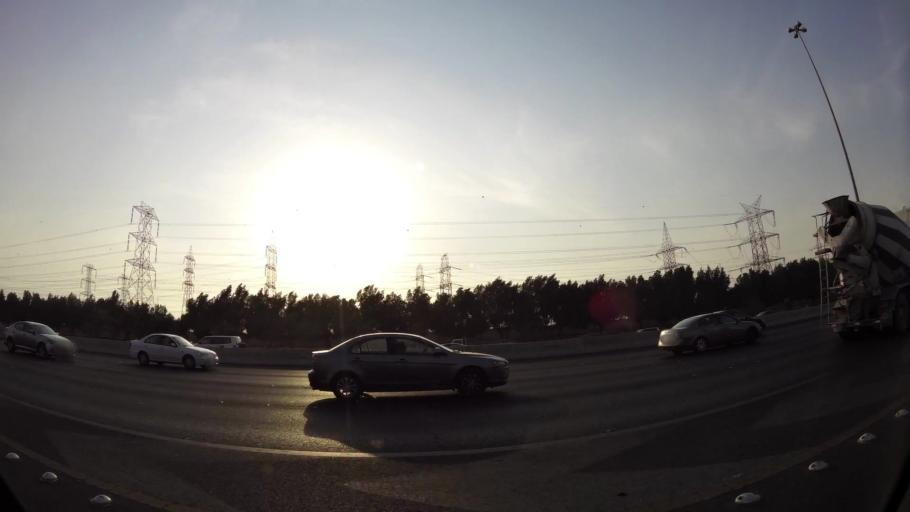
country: KW
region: Mubarak al Kabir
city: Sabah as Salim
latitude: 29.2360
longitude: 48.0513
